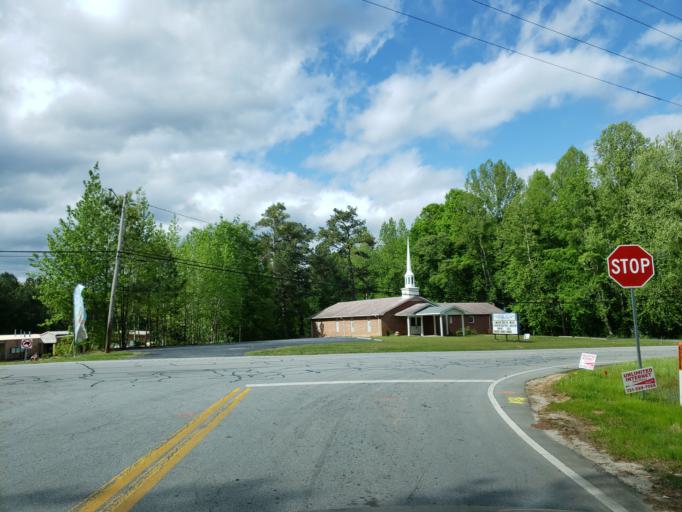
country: US
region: Georgia
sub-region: Haralson County
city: Tallapoosa
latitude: 33.7437
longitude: -85.3023
